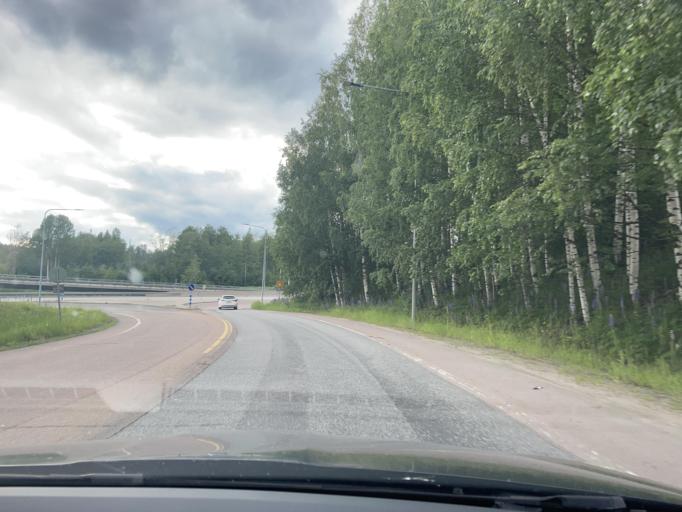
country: FI
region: Central Finland
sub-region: Jyvaeskylae
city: Jyvaeskylae
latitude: 62.2188
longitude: 25.7265
